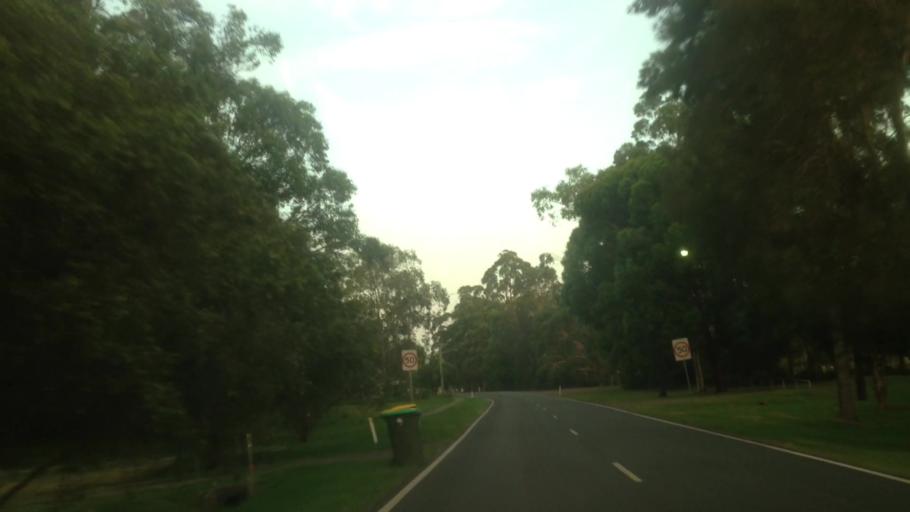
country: AU
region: New South Wales
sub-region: Lake Macquarie Shire
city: Dora Creek
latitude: -33.0818
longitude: 151.4978
